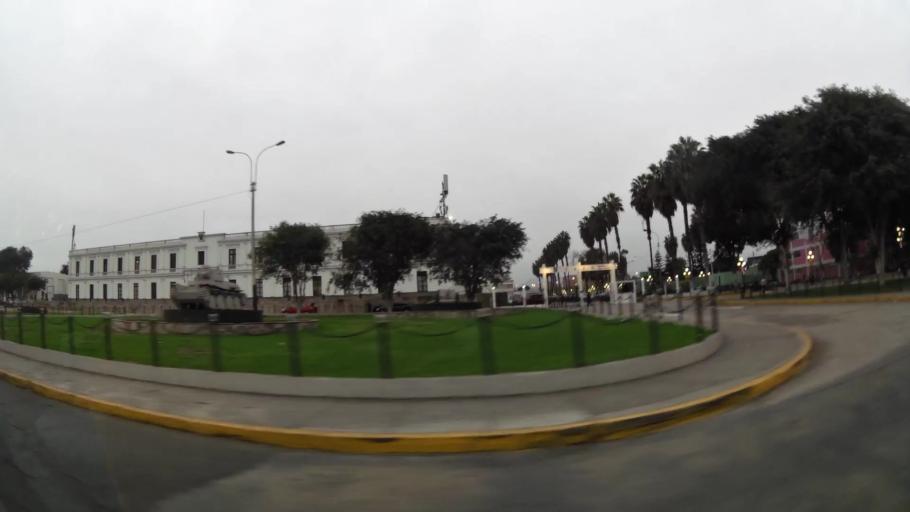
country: PE
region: Lima
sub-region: Lima
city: Surco
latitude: -12.1641
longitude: -77.0219
